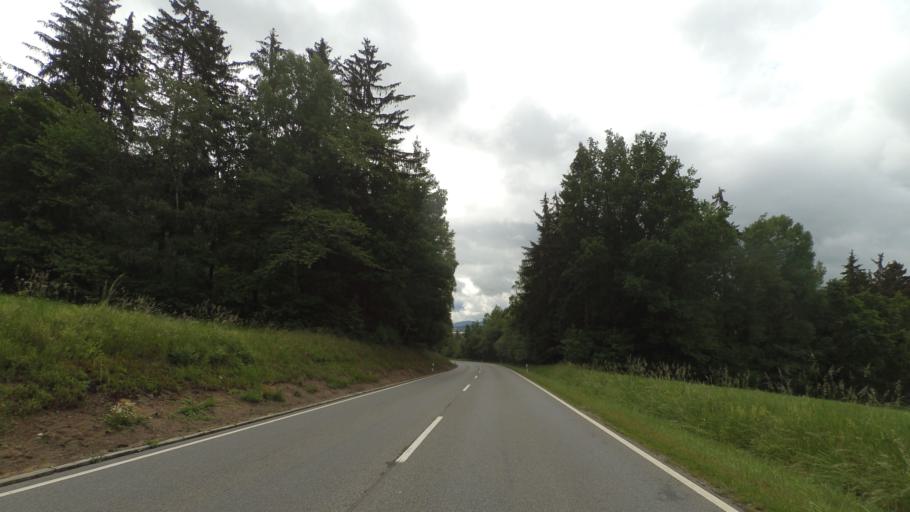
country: DE
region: Bavaria
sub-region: Lower Bavaria
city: Viechtach
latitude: 49.0830
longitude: 12.8574
